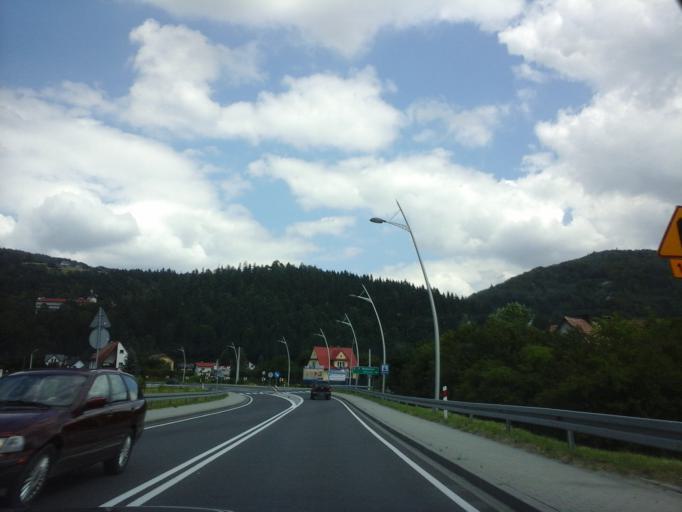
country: PL
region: Lesser Poland Voivodeship
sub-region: Powiat suski
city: Makow Podhalanski
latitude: 49.7226
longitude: 19.6901
